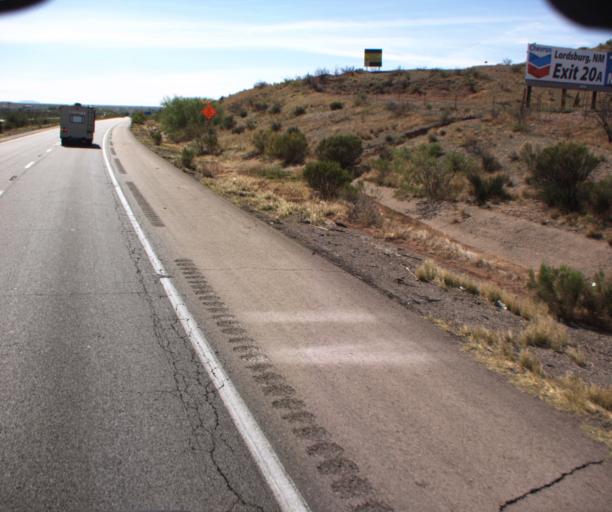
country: US
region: Arizona
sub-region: Cochise County
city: Benson
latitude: 31.9761
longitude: -110.2902
